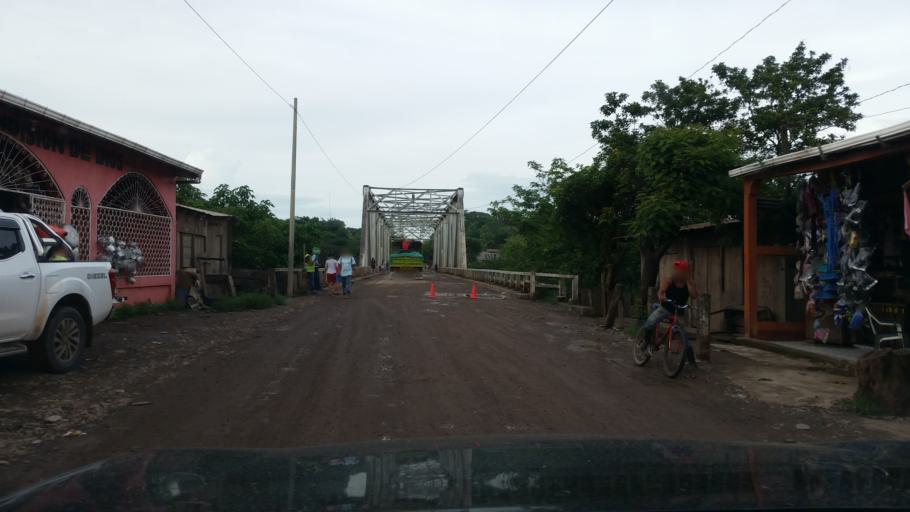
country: NI
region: Matagalpa
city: Rio Blanco
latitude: 13.1722
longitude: -84.9590
